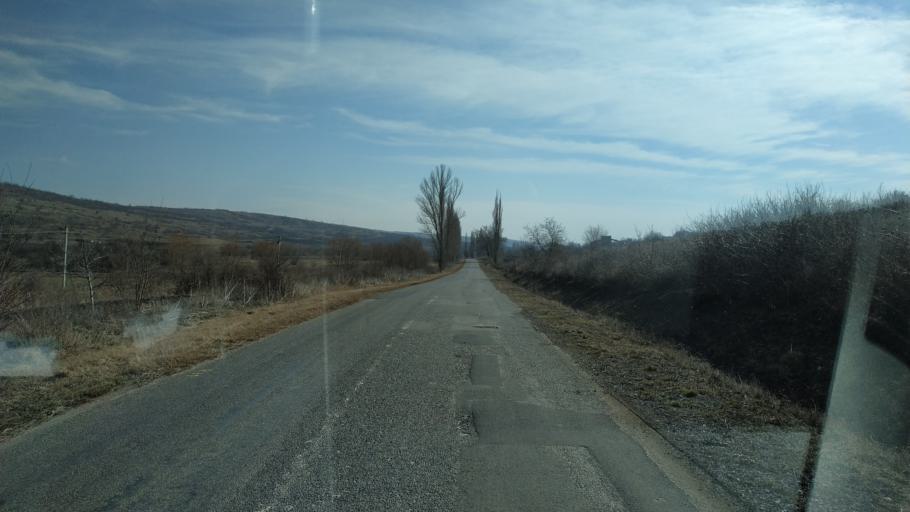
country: MD
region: Nisporeni
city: Nisporeni
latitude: 47.1656
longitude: 28.0996
